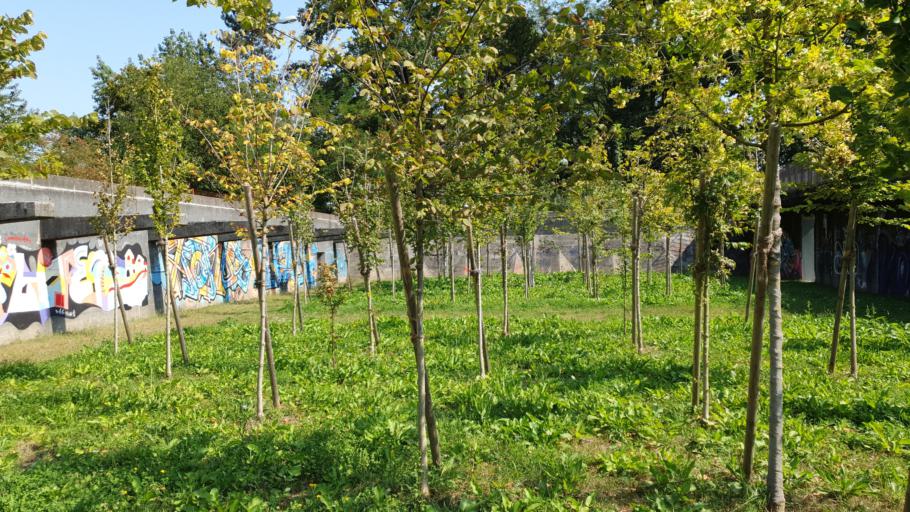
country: CH
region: Solothurn
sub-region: Bezirk Wasseramt
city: Luterbach
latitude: 47.2257
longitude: 7.5825
